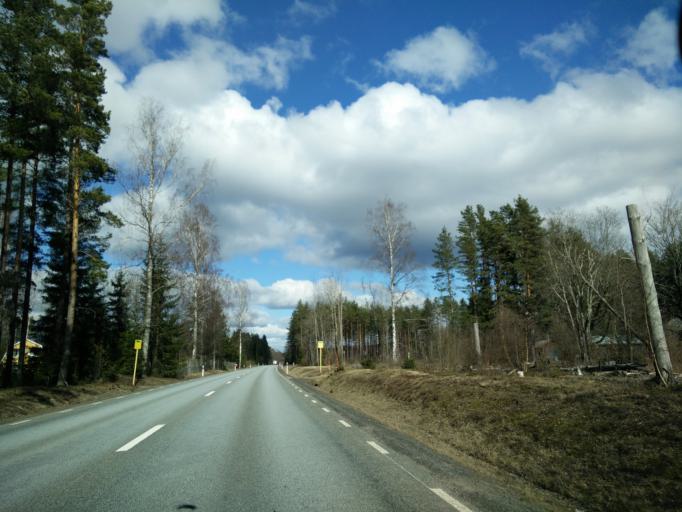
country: SE
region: Vaermland
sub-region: Hagfors Kommun
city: Hagfors
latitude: 59.9785
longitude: 13.5693
